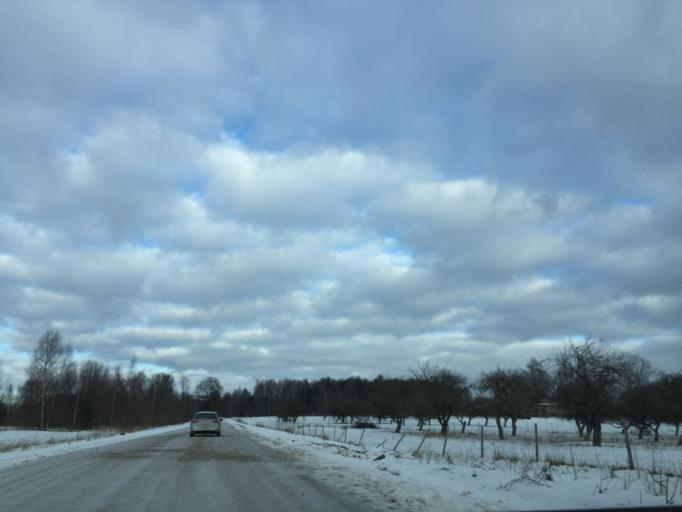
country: LV
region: Lielvarde
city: Lielvarde
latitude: 56.5685
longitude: 24.7334
